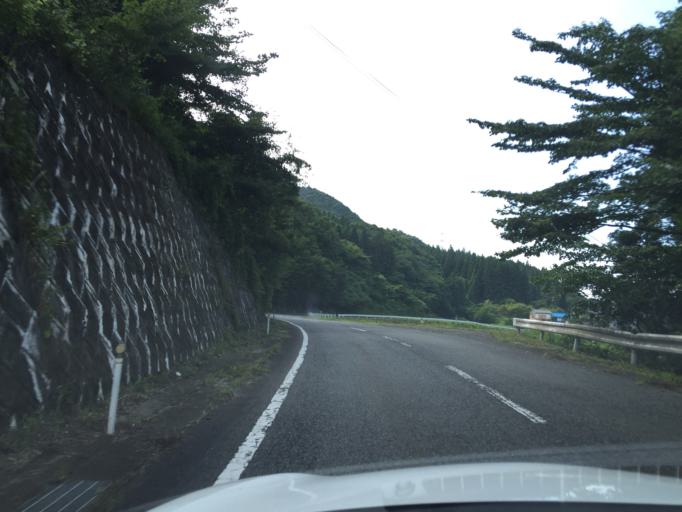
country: JP
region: Fukushima
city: Ishikawa
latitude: 37.1350
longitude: 140.6412
